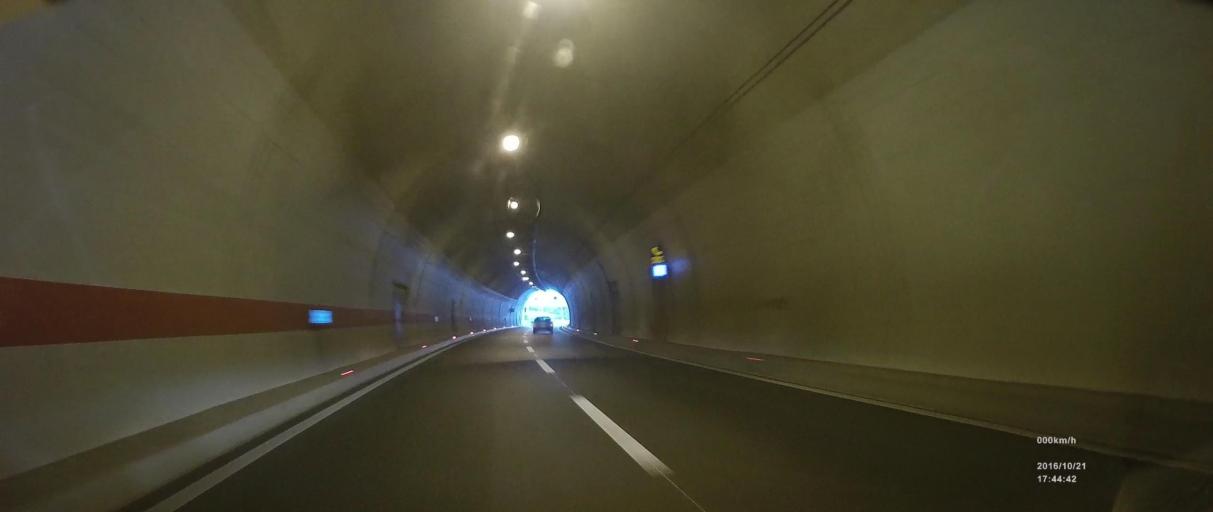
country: HR
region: Primorsko-Goranska
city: Hreljin
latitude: 45.2833
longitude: 14.5901
